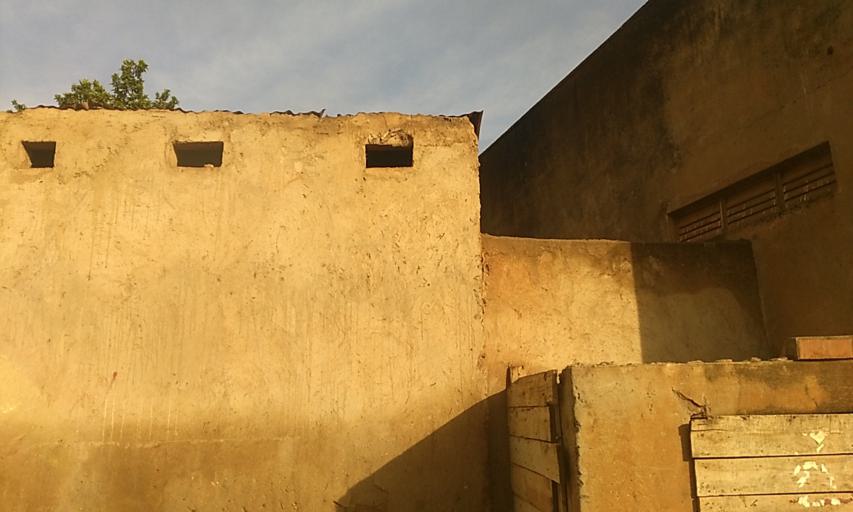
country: UG
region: Central Region
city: Kampala Central Division
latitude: 0.3225
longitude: 32.5721
